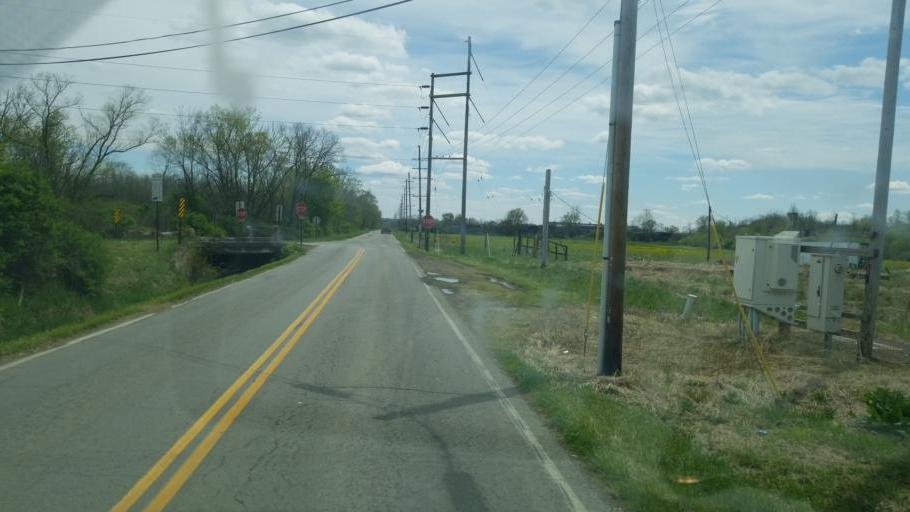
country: US
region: Ohio
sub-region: Wayne County
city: Wooster
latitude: 40.7778
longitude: -81.9443
